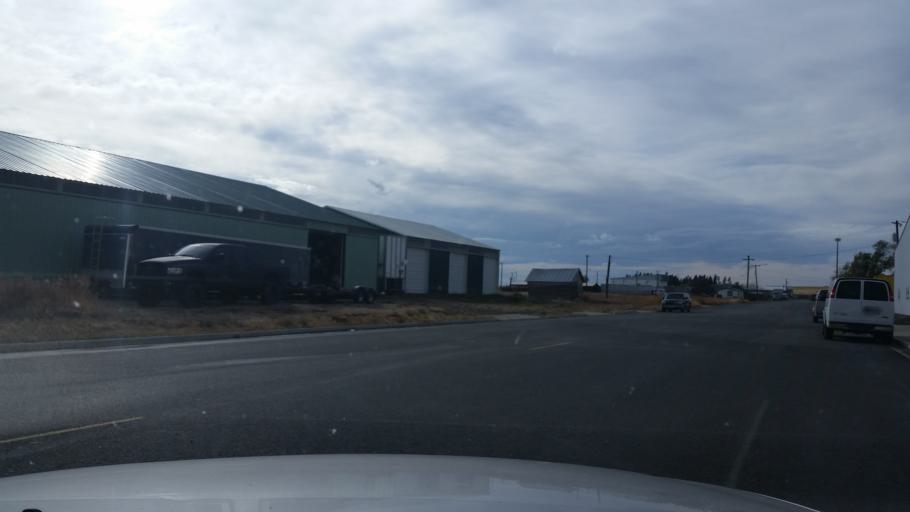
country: US
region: Washington
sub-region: Lincoln County
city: Davenport
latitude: 47.6463
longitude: -118.1526
